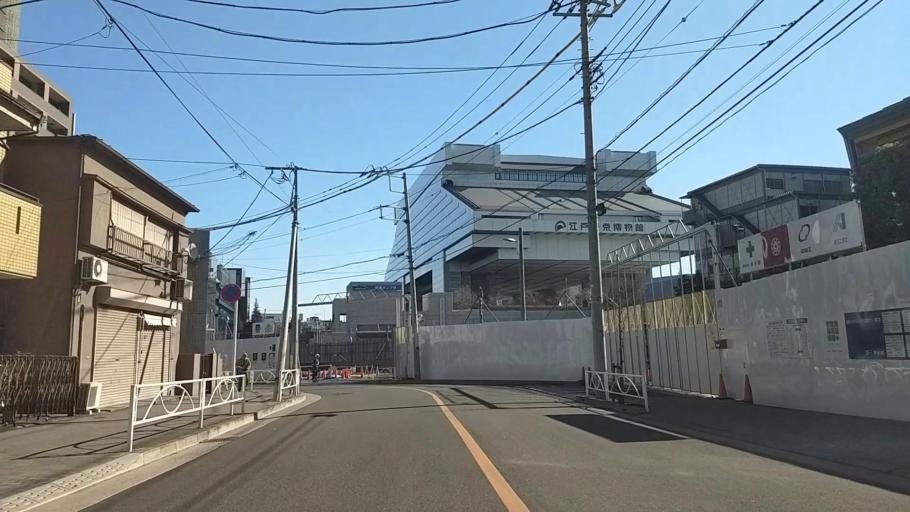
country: JP
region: Tokyo
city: Urayasu
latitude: 35.6977
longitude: 139.7938
